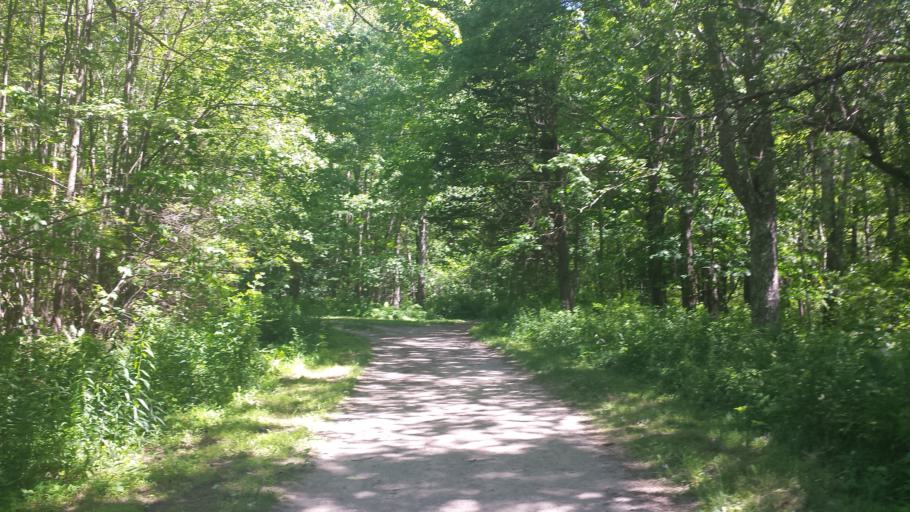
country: US
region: New York
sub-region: Westchester County
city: Pound Ridge
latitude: 41.2474
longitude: -73.5940
